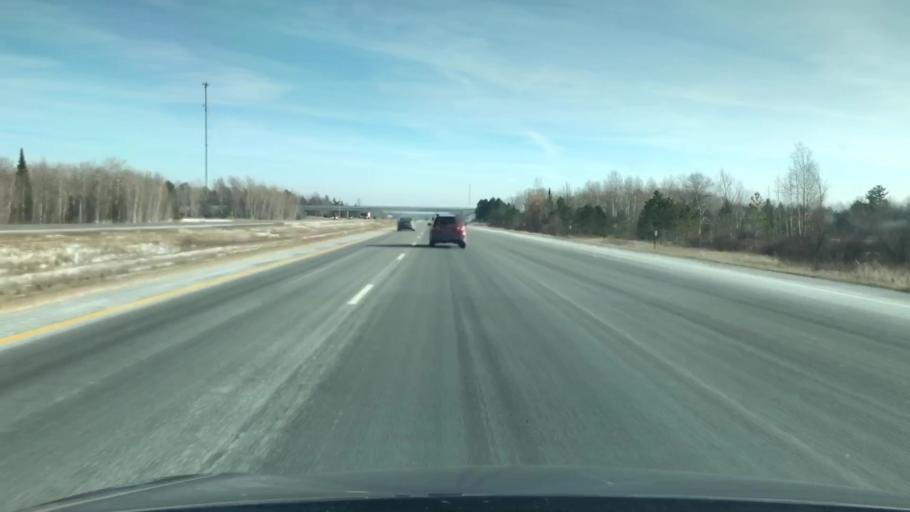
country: US
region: Michigan
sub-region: Roscommon County
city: Saint Helen
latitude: 44.3133
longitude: -84.4981
